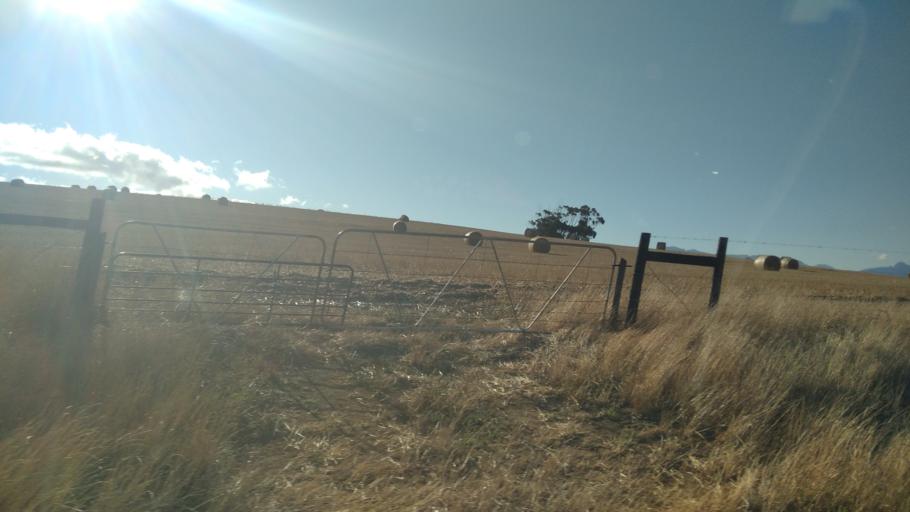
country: ZA
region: Western Cape
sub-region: Overberg District Municipality
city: Caledon
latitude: -34.1361
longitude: 19.2960
